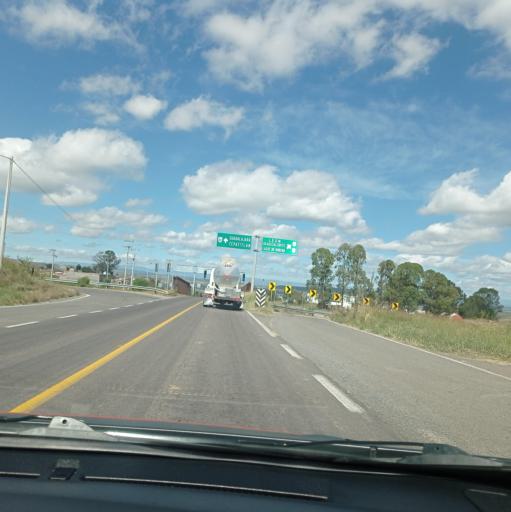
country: MX
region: Jalisco
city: Valle de Guadalupe
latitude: 21.0311
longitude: -102.5534
